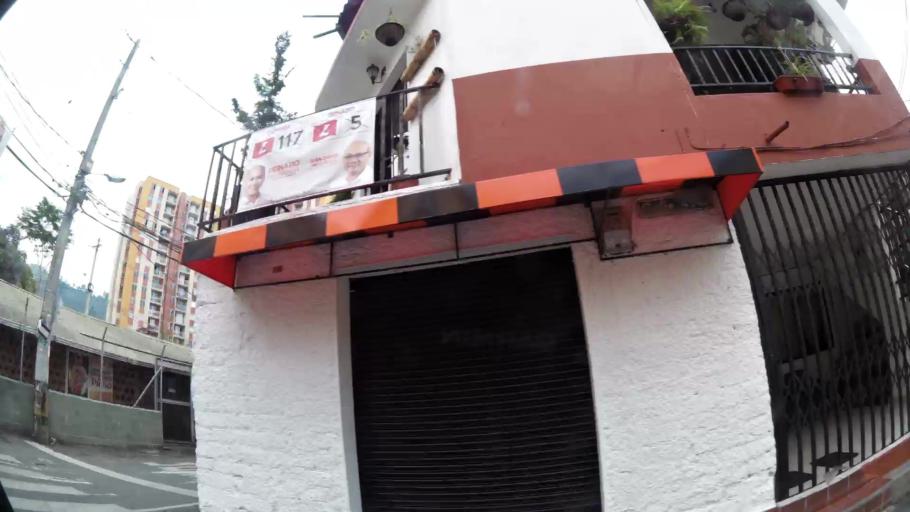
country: CO
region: Antioquia
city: Sabaneta
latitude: 6.1557
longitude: -75.6007
